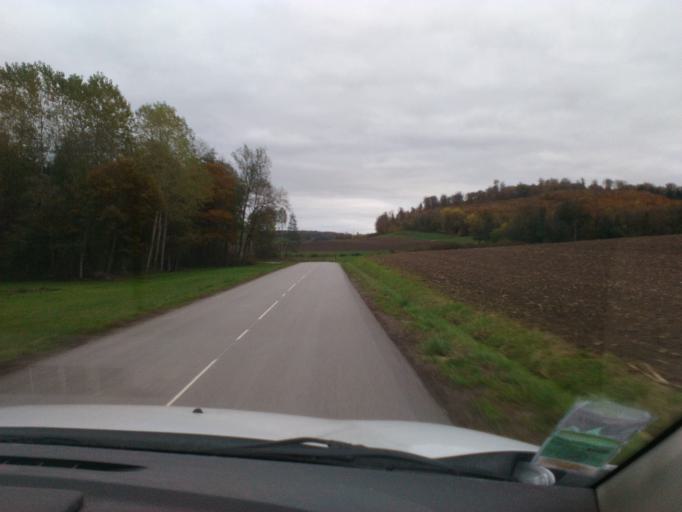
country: FR
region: Lorraine
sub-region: Departement des Vosges
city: Vincey
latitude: 48.2742
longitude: 6.2444
